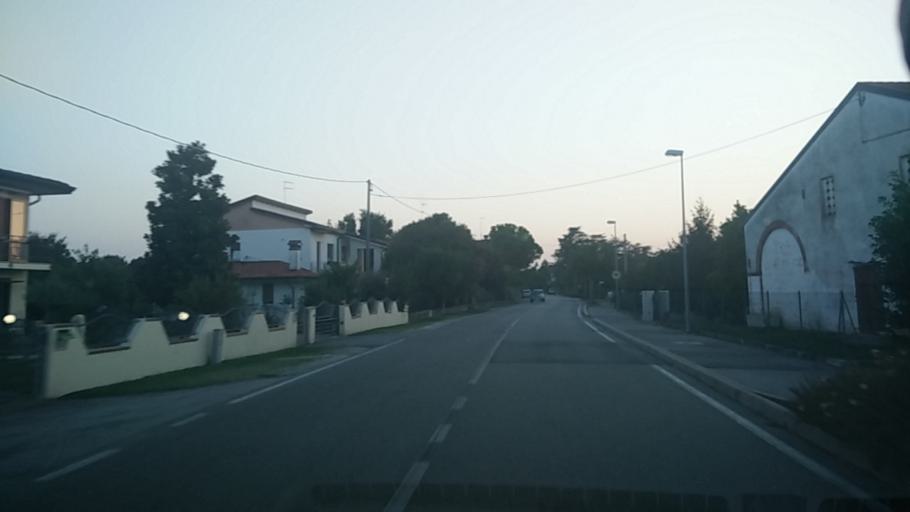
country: IT
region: Veneto
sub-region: Provincia di Venezia
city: San Dona di Piave
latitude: 45.6452
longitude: 12.5672
